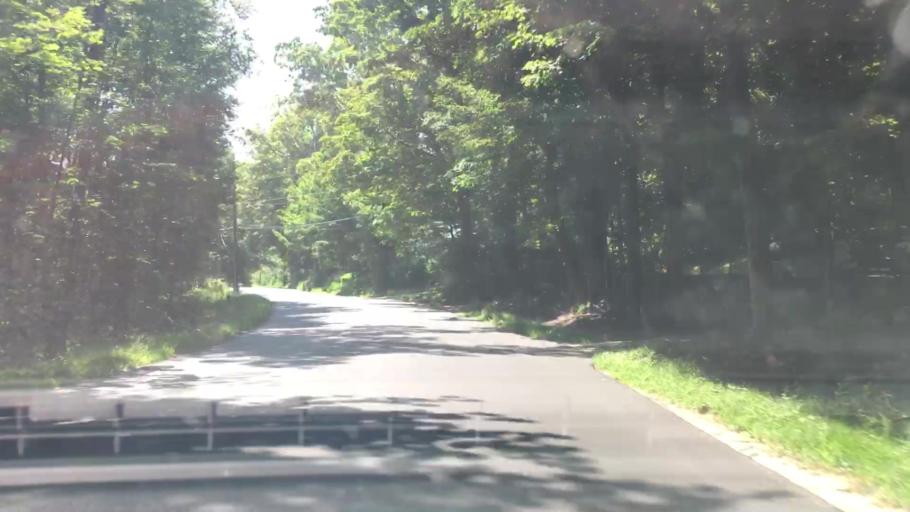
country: US
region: New Hampshire
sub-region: Rockingham County
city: Hampstead
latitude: 42.8769
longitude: -71.2187
